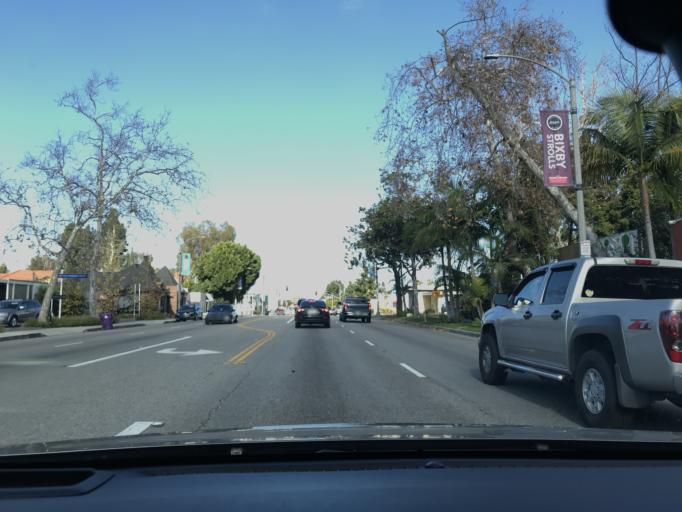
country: US
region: California
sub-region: Los Angeles County
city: Signal Hill
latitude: 33.8275
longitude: -118.1893
